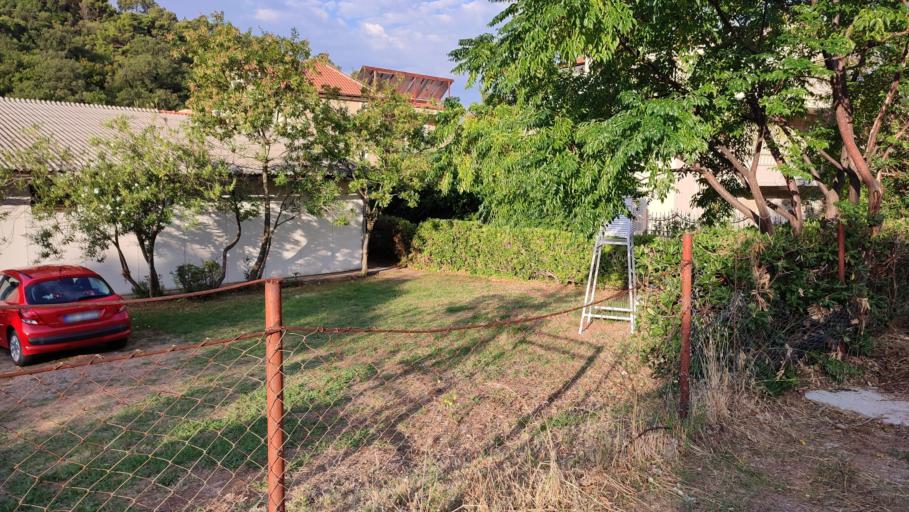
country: ME
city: Petrovac na Moru
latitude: 42.2041
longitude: 18.9476
